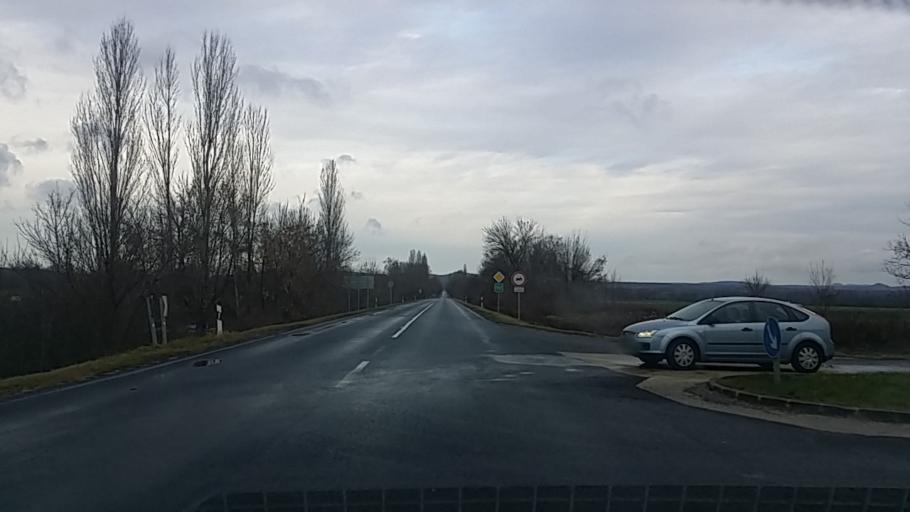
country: HU
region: Veszprem
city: Tapolca
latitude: 46.8454
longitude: 17.3710
